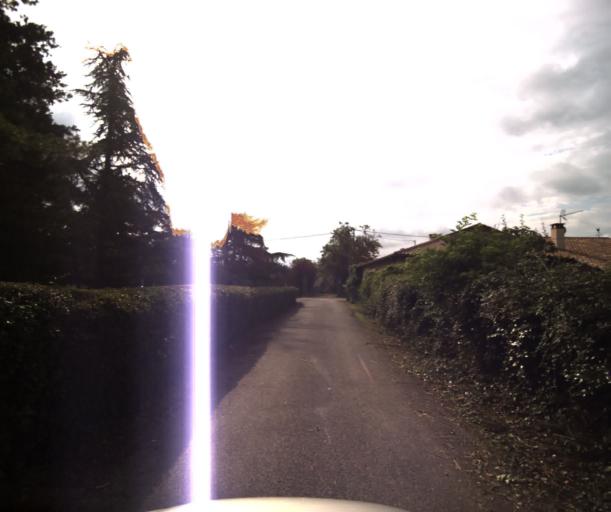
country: FR
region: Midi-Pyrenees
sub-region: Departement de la Haute-Garonne
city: Le Fauga
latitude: 43.4400
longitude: 1.2908
